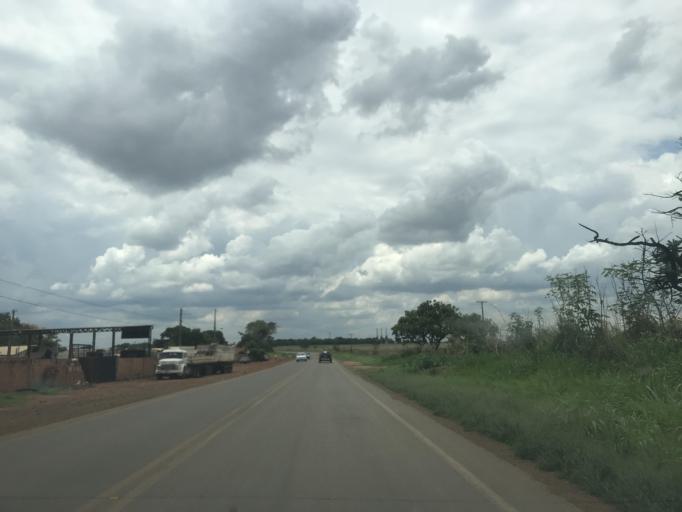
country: BR
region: Goias
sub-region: Vianopolis
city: Vianopolis
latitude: -16.7372
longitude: -48.4989
